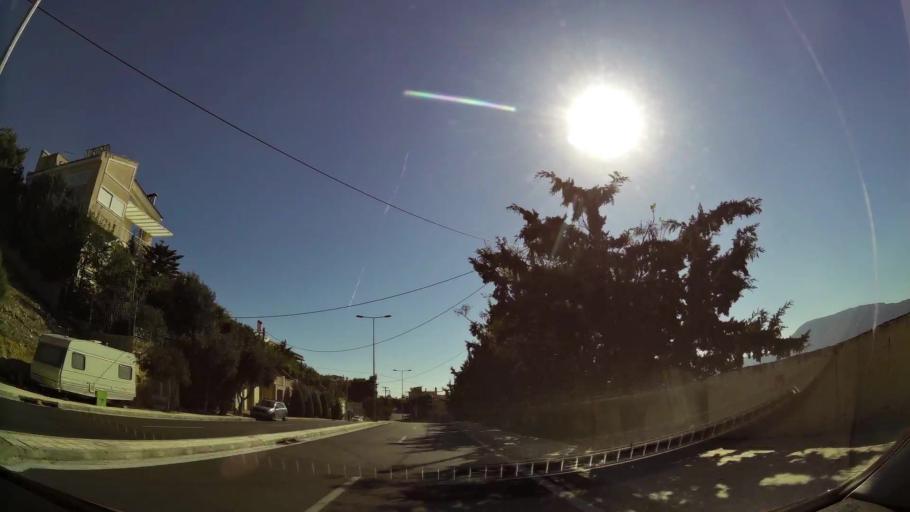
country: GR
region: Attica
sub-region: Nomarchia Anatolikis Attikis
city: Dhrafi
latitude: 38.0041
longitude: 23.9132
